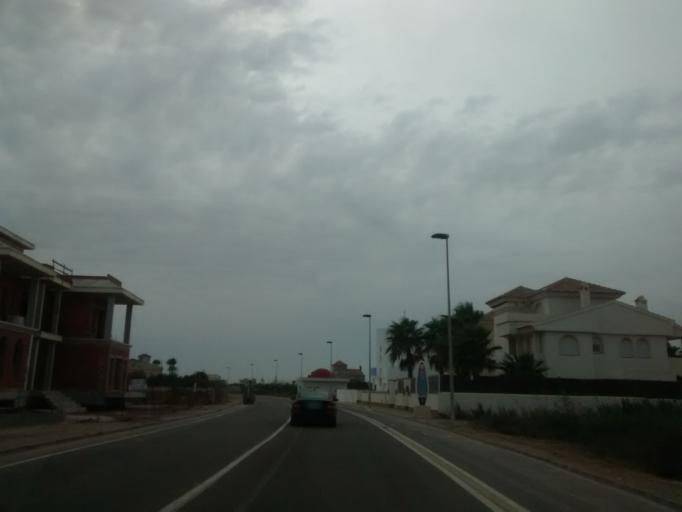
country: ES
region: Murcia
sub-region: Murcia
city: San Pedro del Pinatar
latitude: 37.7785
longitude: -0.7465
